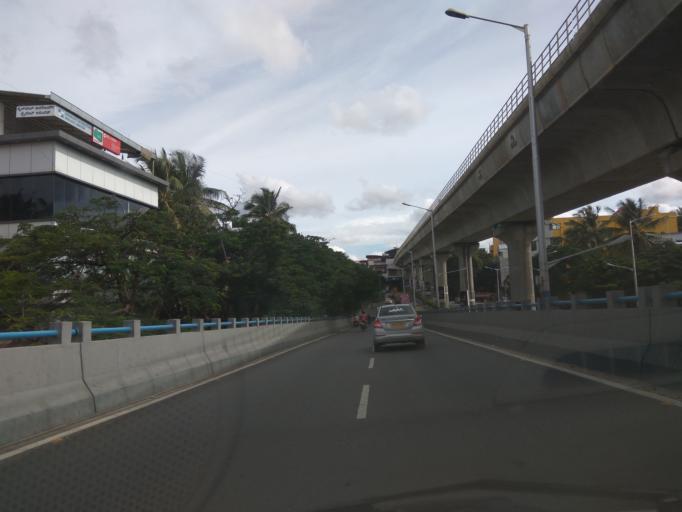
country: IN
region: Karnataka
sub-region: Bangalore Urban
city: Bangalore
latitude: 13.0031
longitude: 77.5495
